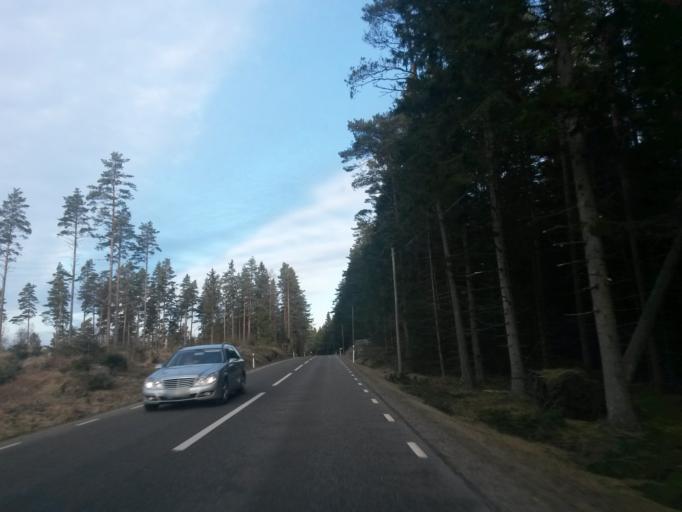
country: SE
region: Vaestra Goetaland
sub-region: Boras Kommun
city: Boras
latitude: 57.8834
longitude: 12.9287
